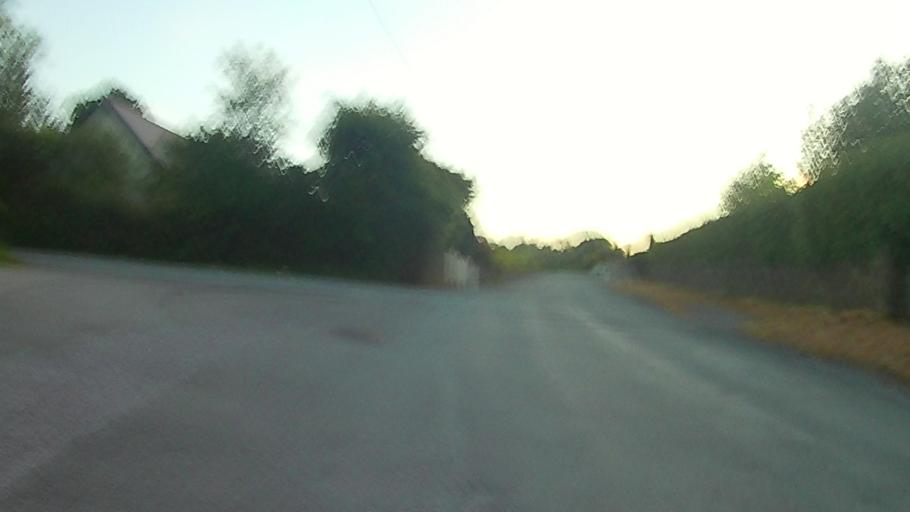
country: IE
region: Munster
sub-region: County Cork
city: Midleton
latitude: 51.9729
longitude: -8.2214
